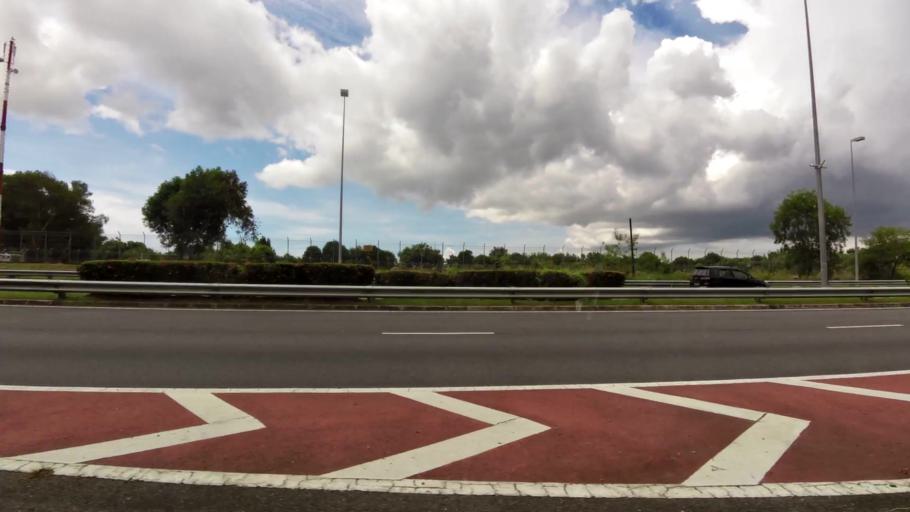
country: BN
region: Brunei and Muara
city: Bandar Seri Begawan
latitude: 4.9555
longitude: 114.9006
